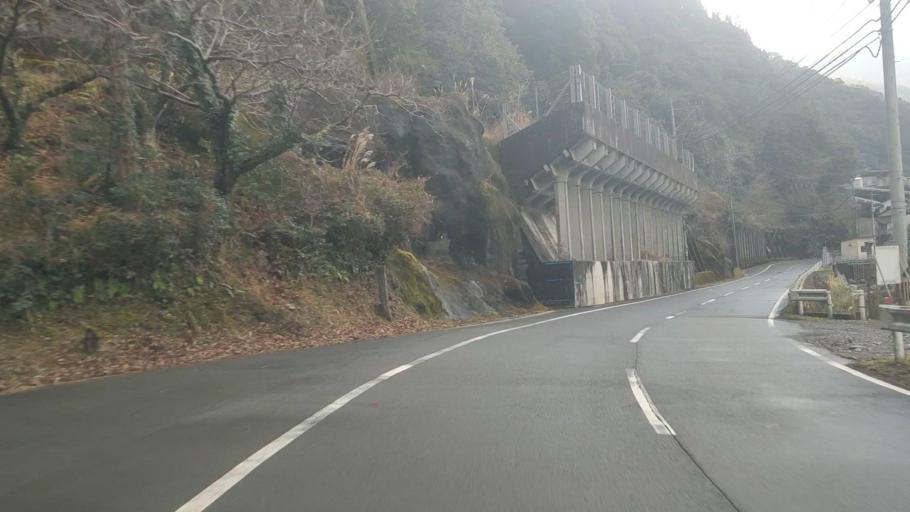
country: JP
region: Kumamoto
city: Hitoyoshi
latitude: 32.4287
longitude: 130.8584
